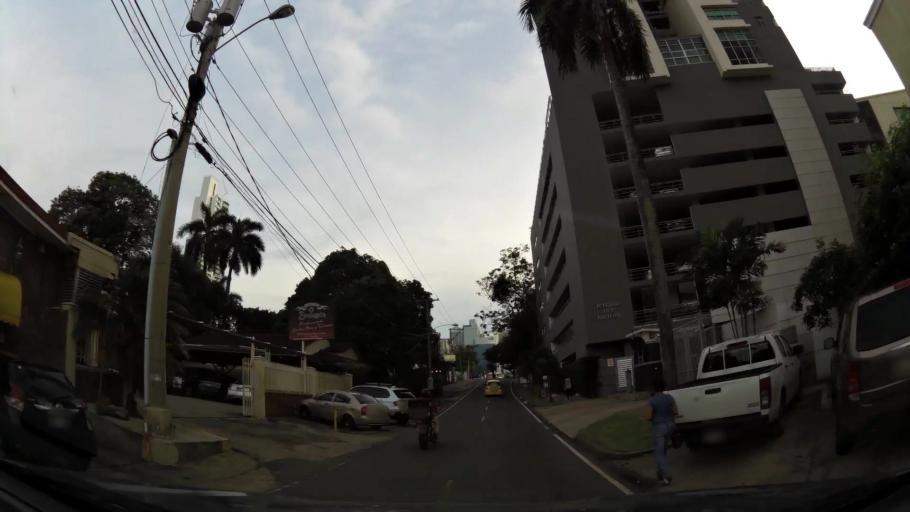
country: PA
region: Panama
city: Panama
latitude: 8.9890
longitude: -79.5108
